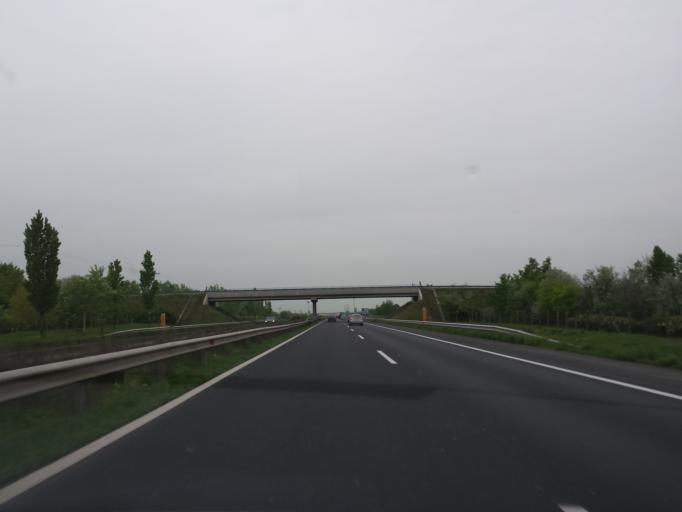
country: HU
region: Gyor-Moson-Sopron
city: Mosonmagyarovar
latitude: 47.8666
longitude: 17.2255
